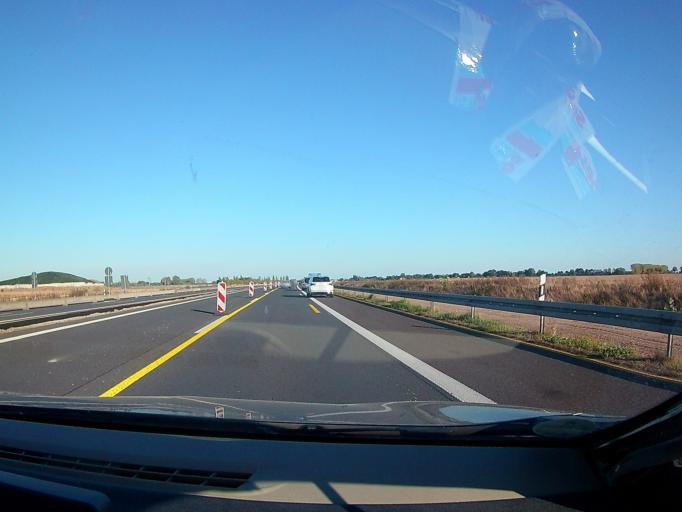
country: DE
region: Brandenburg
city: Velten
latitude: 52.7076
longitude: 13.1117
